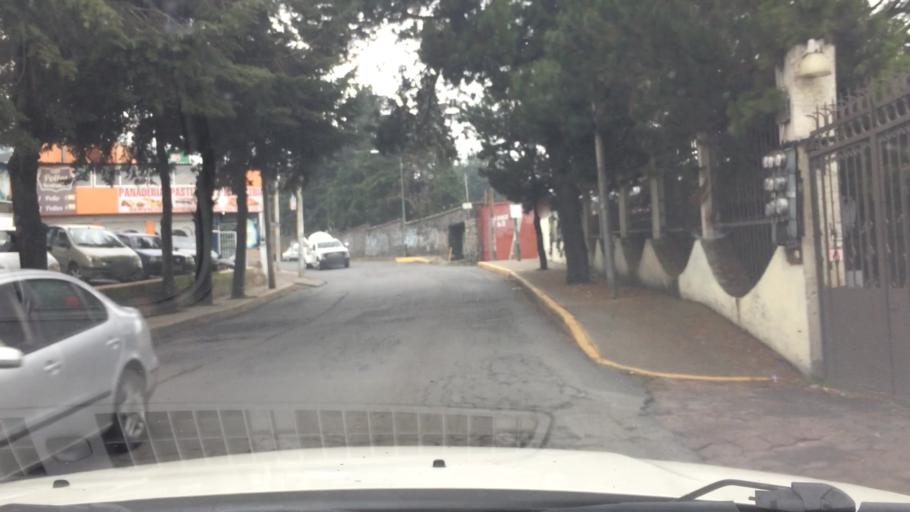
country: MX
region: Mexico City
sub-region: Tlalpan
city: Lomas de Tepemecatl
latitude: 19.2295
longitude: -99.1961
